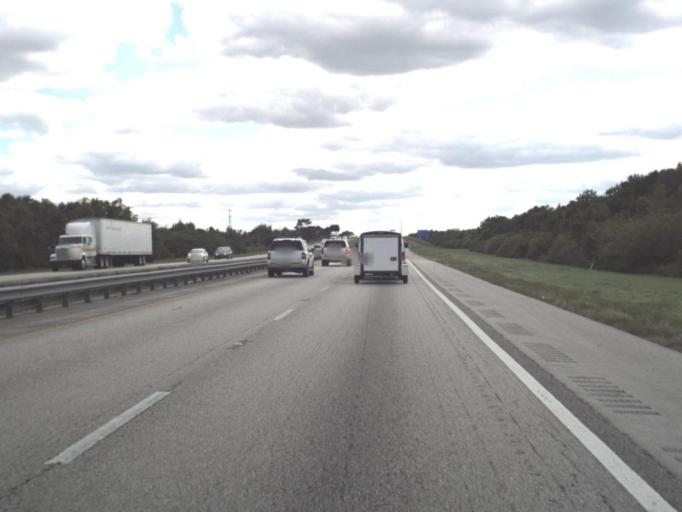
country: US
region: Florida
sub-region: Osceola County
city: Saint Cloud
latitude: 28.2711
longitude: -81.3346
